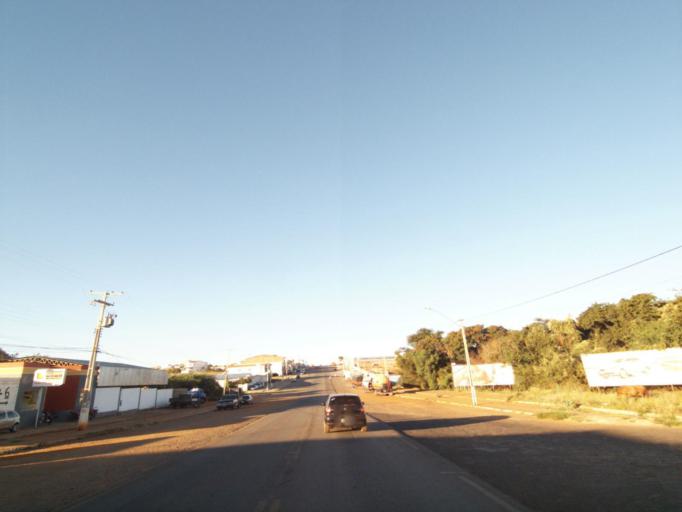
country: BR
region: Bahia
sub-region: Brumado
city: Brumado
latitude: -14.2190
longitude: -41.6870
